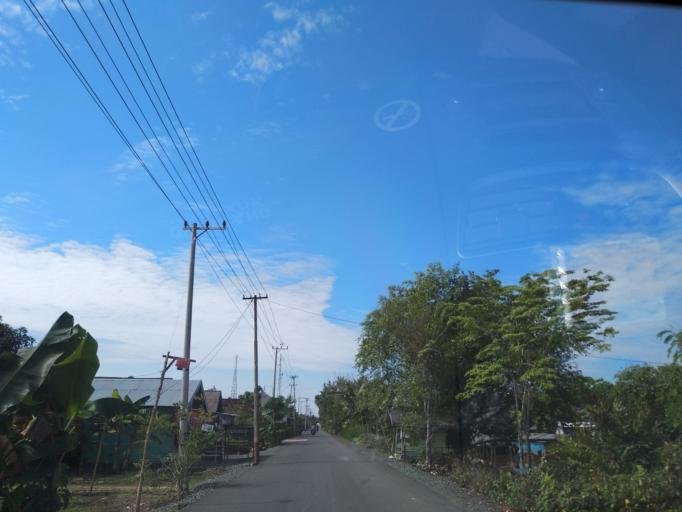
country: ID
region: South Kalimantan
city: Tabunganen
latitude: -3.3267
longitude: 114.4782
